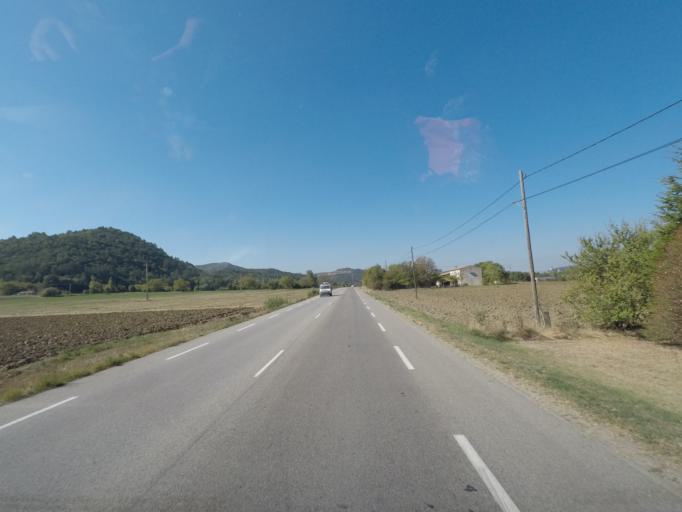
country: FR
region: Rhone-Alpes
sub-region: Departement de la Drome
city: Aouste-sur-Sye
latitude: 44.7090
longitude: 5.0725
